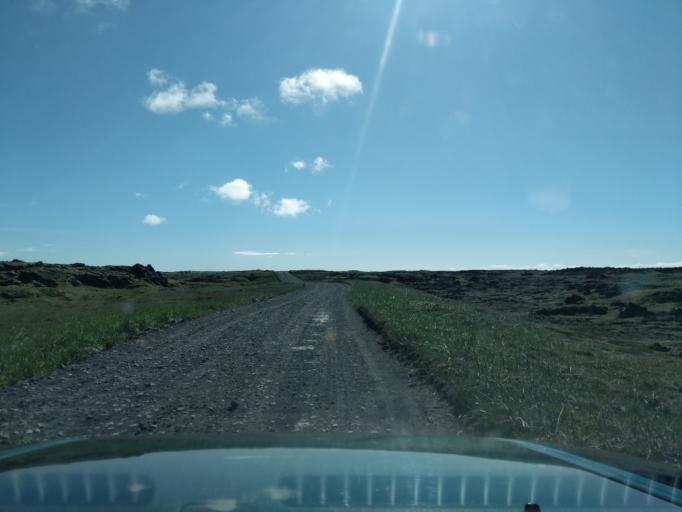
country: IS
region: West
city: Olafsvik
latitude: 64.8760
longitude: -23.9980
